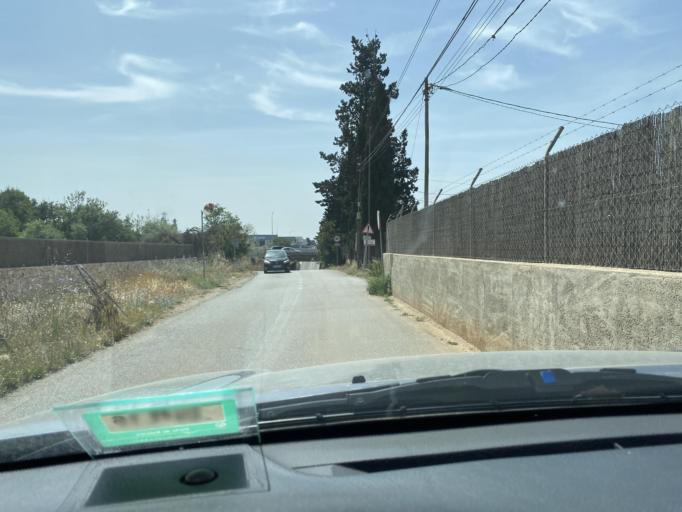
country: ES
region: Balearic Islands
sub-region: Illes Balears
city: Marratxi
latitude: 39.6237
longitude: 2.7106
